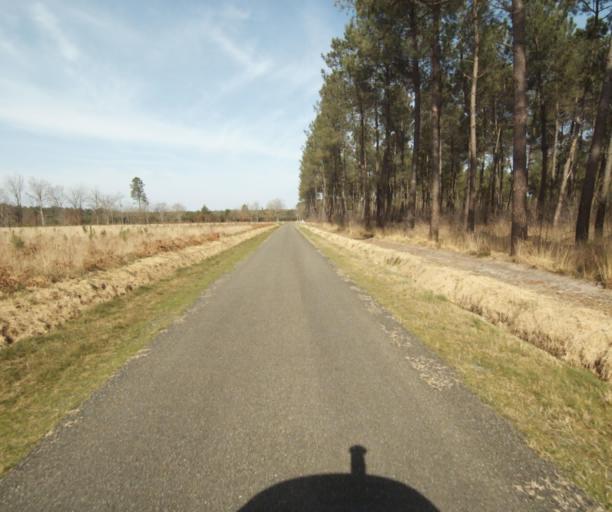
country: FR
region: Aquitaine
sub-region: Departement de la Gironde
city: Bazas
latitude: 44.2161
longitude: -0.2045
